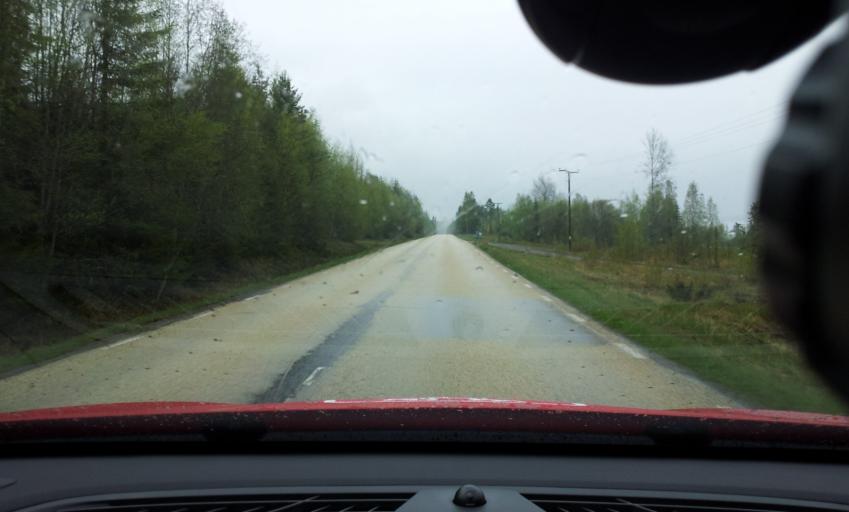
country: SE
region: Jaemtland
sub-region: Bergs Kommun
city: Hoverberg
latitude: 62.8668
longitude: 14.3739
